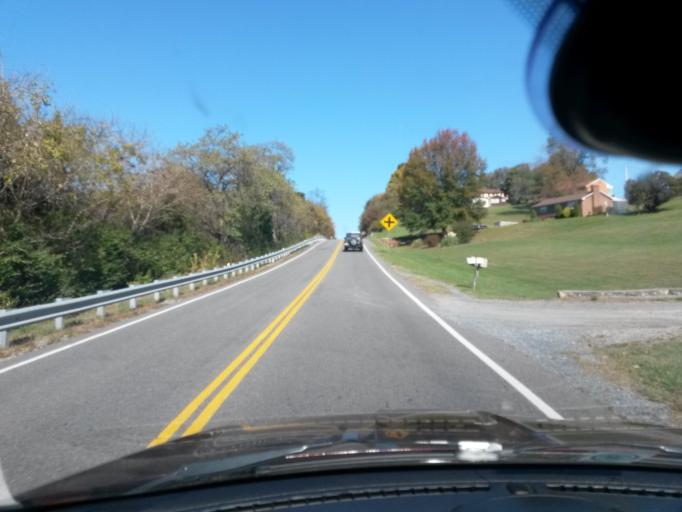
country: US
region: Virginia
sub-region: City of Roanoke
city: Cedar Bluff
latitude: 37.2387
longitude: -79.9102
